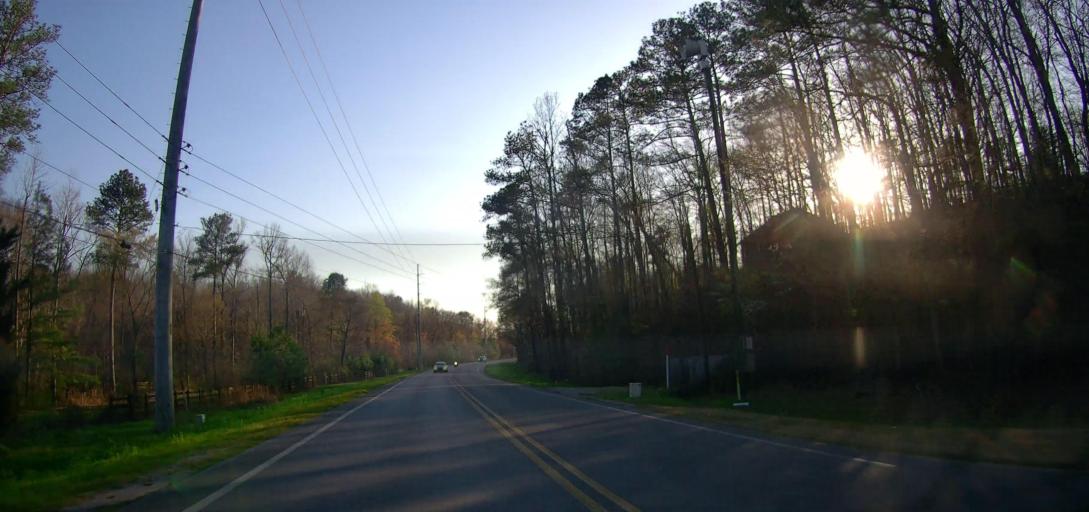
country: US
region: Alabama
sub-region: Shelby County
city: Indian Springs Village
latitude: 33.2960
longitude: -86.7496
